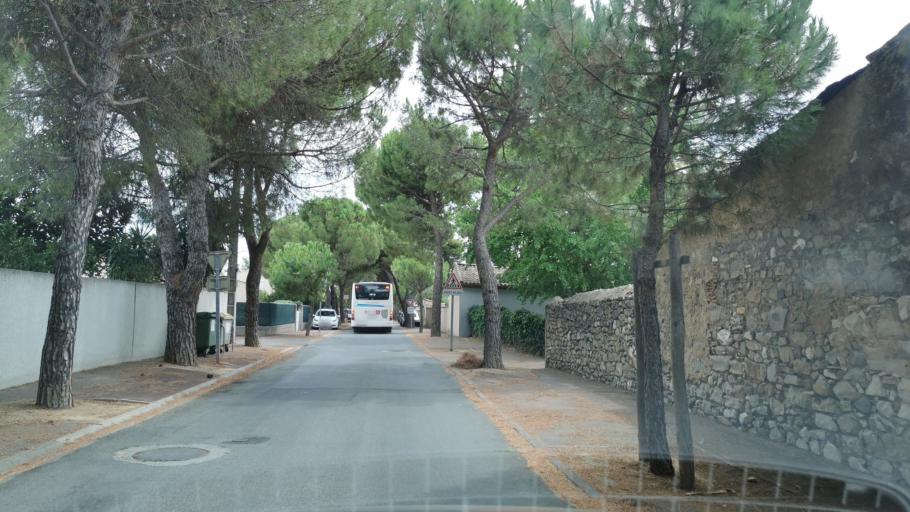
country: FR
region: Languedoc-Roussillon
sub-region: Departement de l'Aude
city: Argeliers
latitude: 43.3073
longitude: 2.9156
